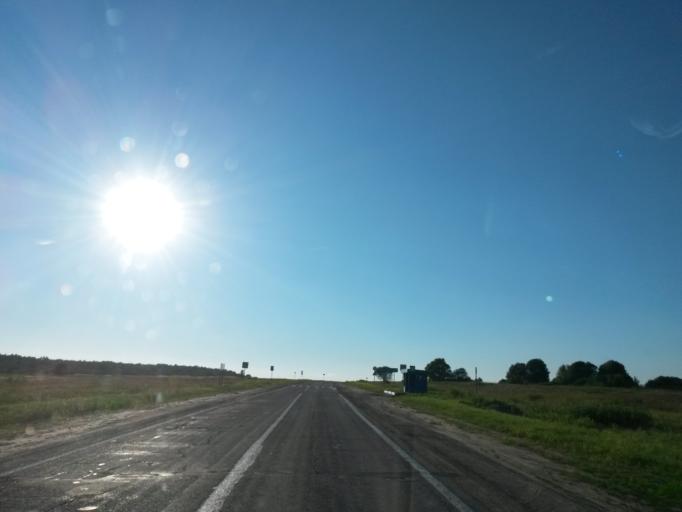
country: RU
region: Jaroslavl
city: Gavrilov-Yam
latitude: 57.2821
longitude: 39.9043
